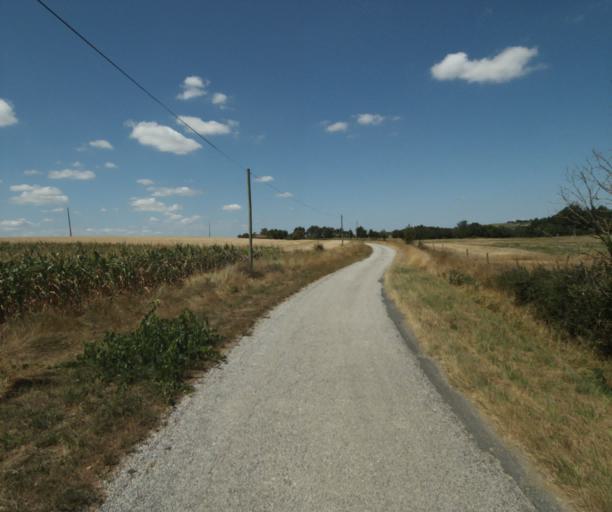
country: FR
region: Midi-Pyrenees
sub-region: Departement de la Haute-Garonne
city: Auriac-sur-Vendinelle
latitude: 43.5016
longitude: 1.8455
